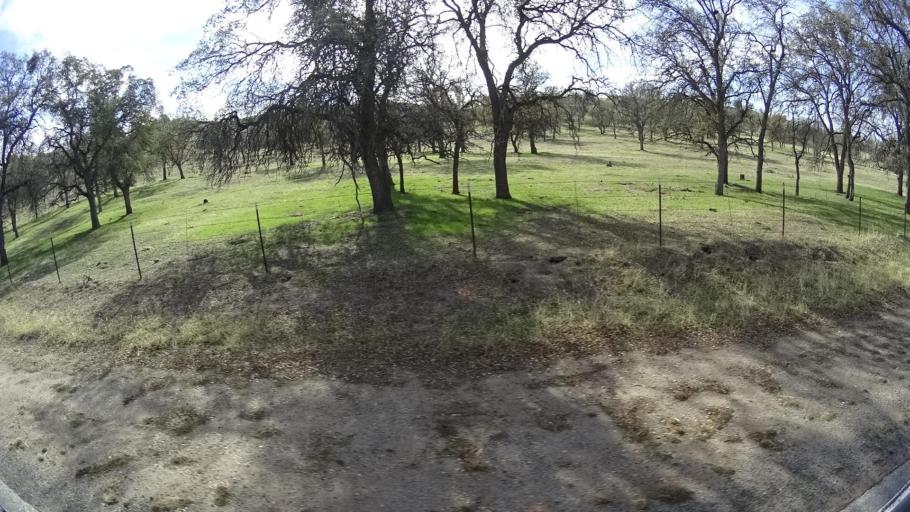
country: US
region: California
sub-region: Kern County
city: Oildale
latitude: 35.6271
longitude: -118.8312
